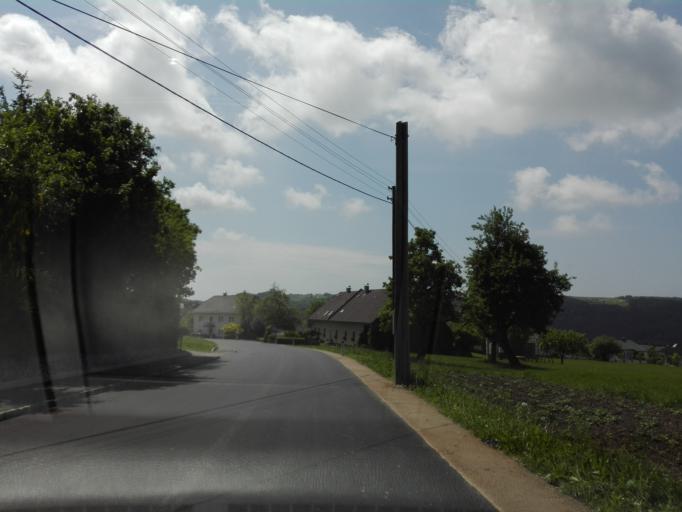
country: AT
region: Upper Austria
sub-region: Politischer Bezirk Rohrbach
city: Atzesberg
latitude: 48.4148
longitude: 13.9147
